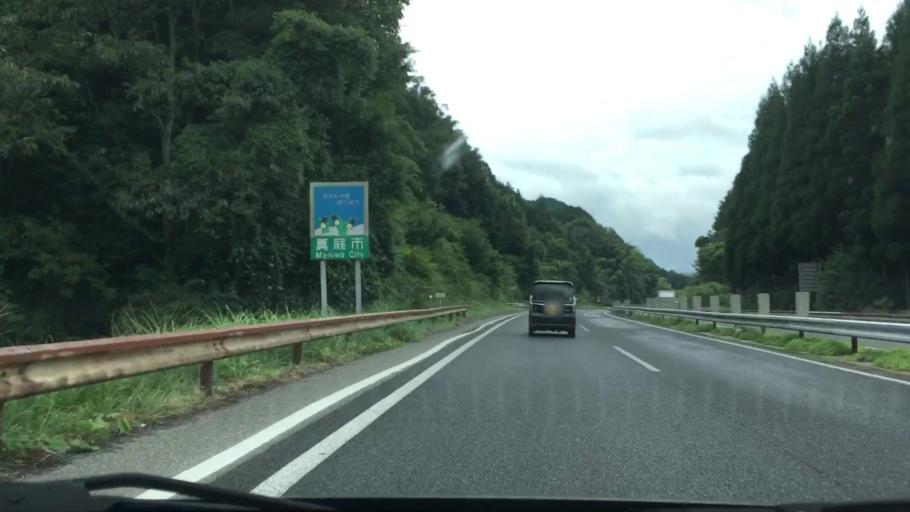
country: JP
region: Okayama
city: Tsuyama
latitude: 35.0575
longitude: 133.8242
